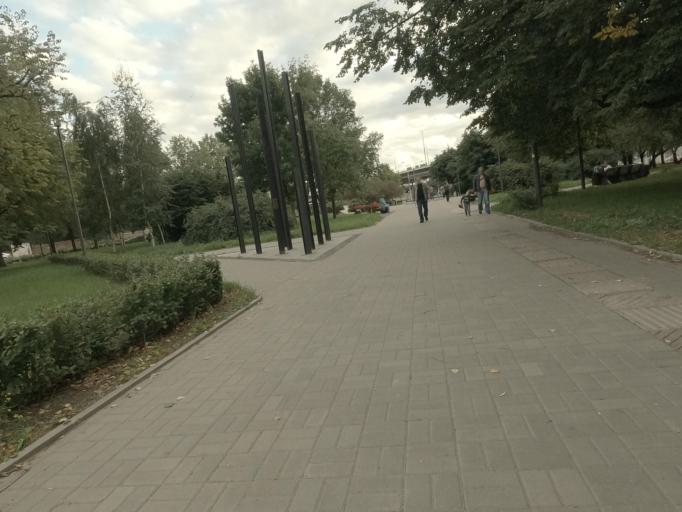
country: RU
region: St.-Petersburg
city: Avtovo
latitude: 59.8654
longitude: 30.2634
